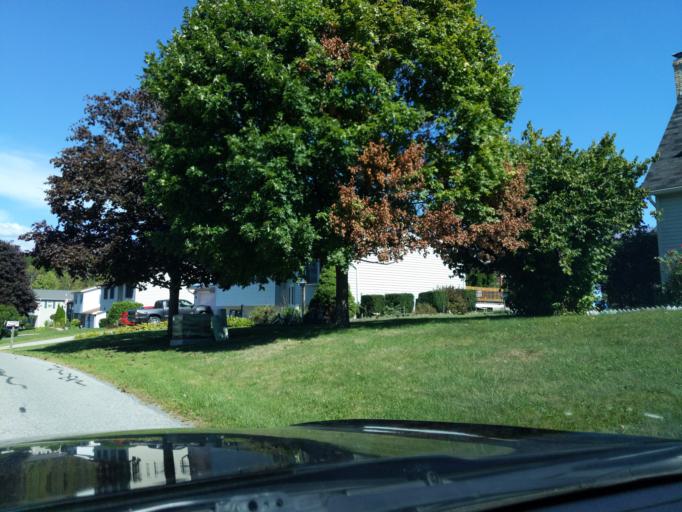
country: US
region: Pennsylvania
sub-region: Blair County
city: Greenwood
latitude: 40.5357
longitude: -78.3632
